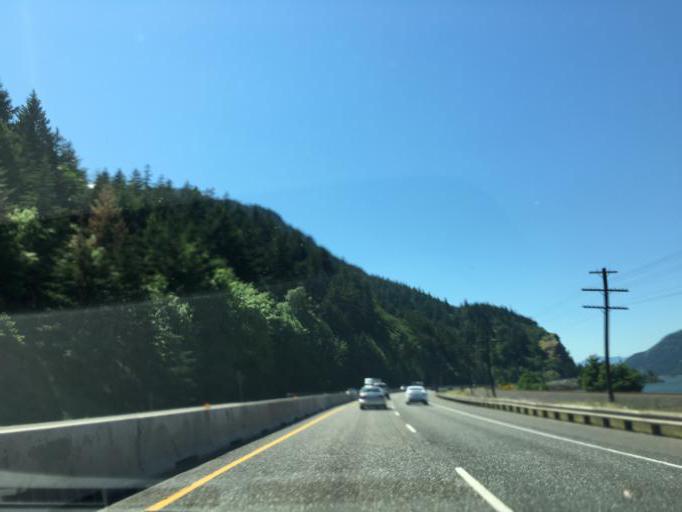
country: US
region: Oregon
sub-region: Hood River County
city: Hood River
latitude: 45.7002
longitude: -121.6287
